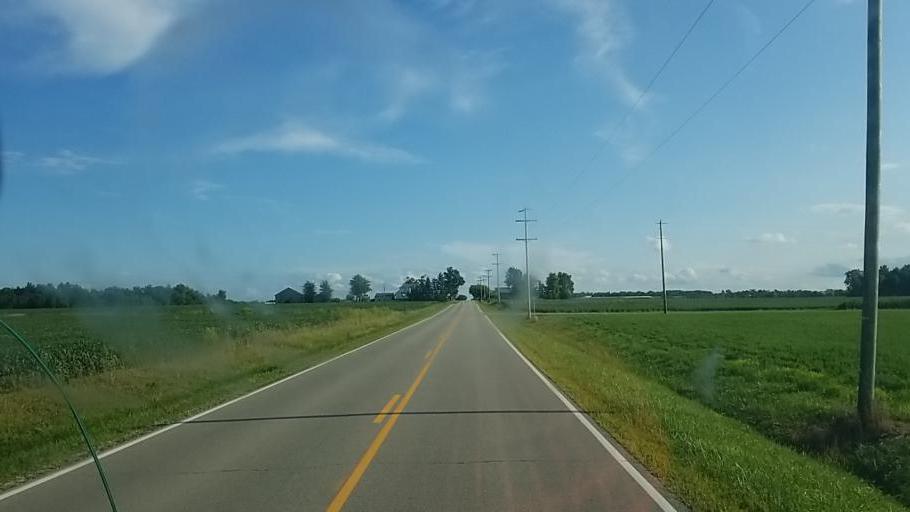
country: US
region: Ohio
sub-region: Crawford County
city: Bucyrus
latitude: 40.8273
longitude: -83.0931
